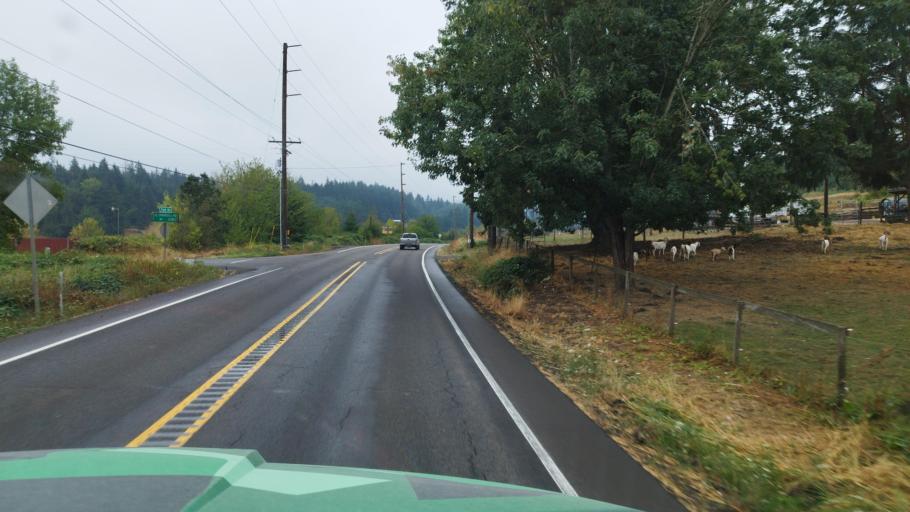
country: US
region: Oregon
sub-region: Yamhill County
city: Yamhill
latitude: 45.4044
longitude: -123.1235
